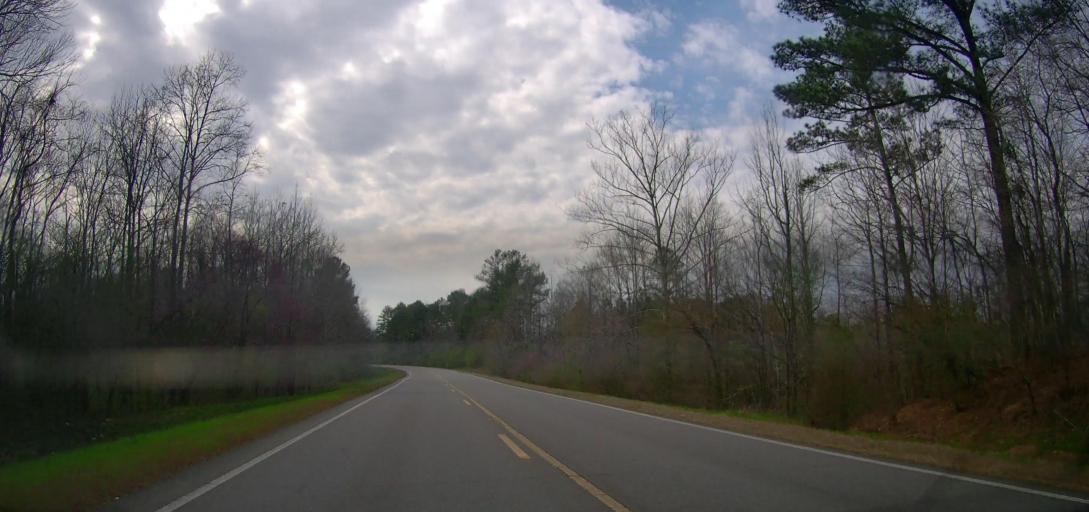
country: US
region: Alabama
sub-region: Marion County
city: Winfield
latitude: 33.9357
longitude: -87.7214
